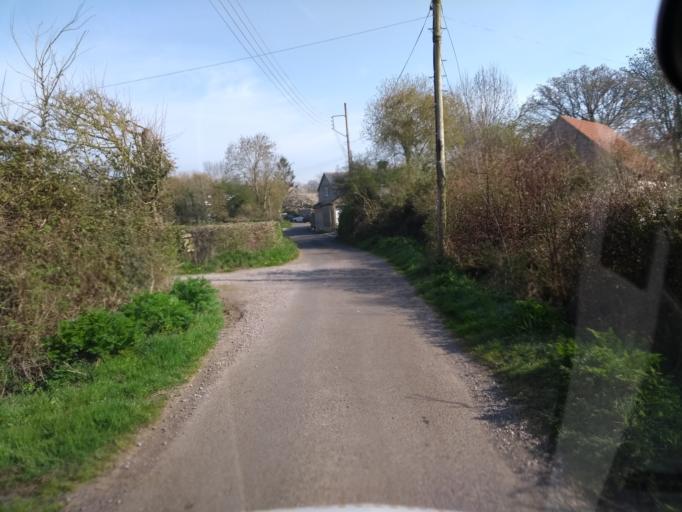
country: GB
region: England
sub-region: Somerset
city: Creech Saint Michael
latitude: 50.9753
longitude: -2.9908
